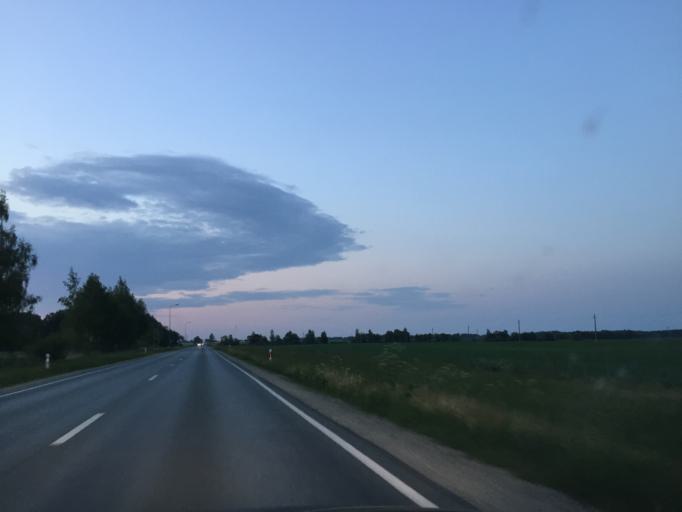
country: LT
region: Siauliu apskritis
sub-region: Joniskis
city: Joniskis
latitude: 56.1168
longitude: 23.4952
